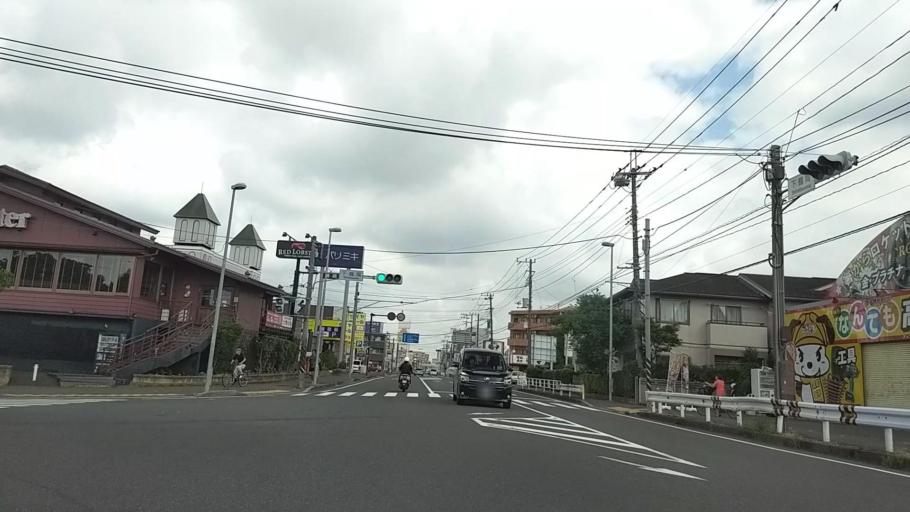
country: JP
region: Kanagawa
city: Minami-rinkan
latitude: 35.5045
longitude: 139.4644
